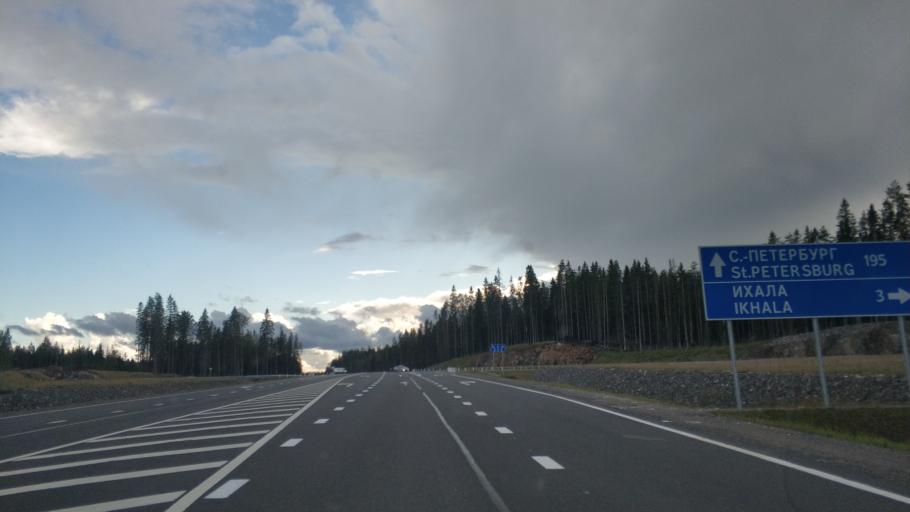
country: RU
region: Republic of Karelia
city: Lakhdenpokh'ya
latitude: 61.4665
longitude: 30.0013
